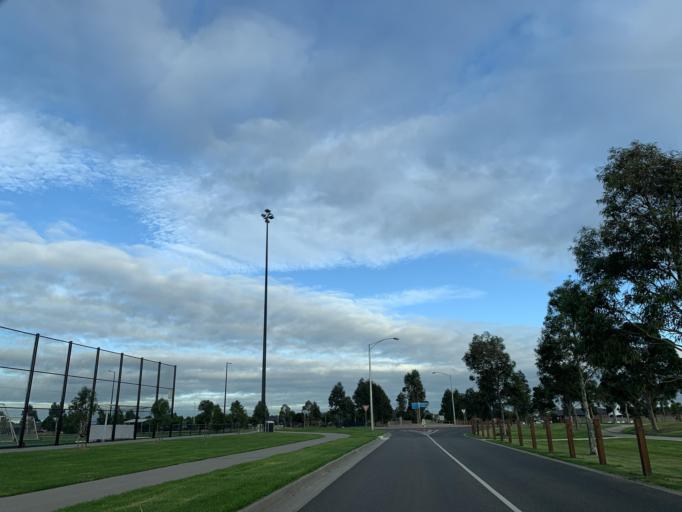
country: AU
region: Victoria
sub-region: Casey
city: Cranbourne East
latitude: -38.1228
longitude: 145.3085
